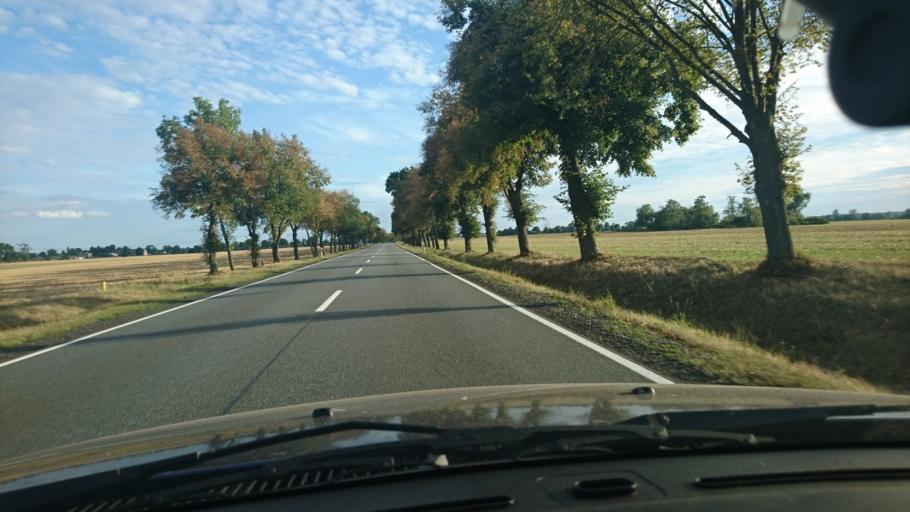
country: PL
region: Opole Voivodeship
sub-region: Powiat kluczborski
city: Kluczbork
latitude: 51.0381
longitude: 18.1943
